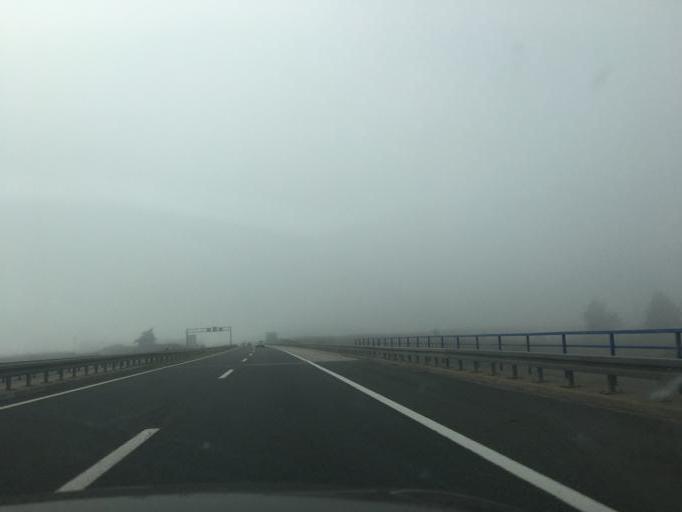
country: HR
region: Licko-Senjska
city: Gospic
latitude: 44.5660
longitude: 15.4267
